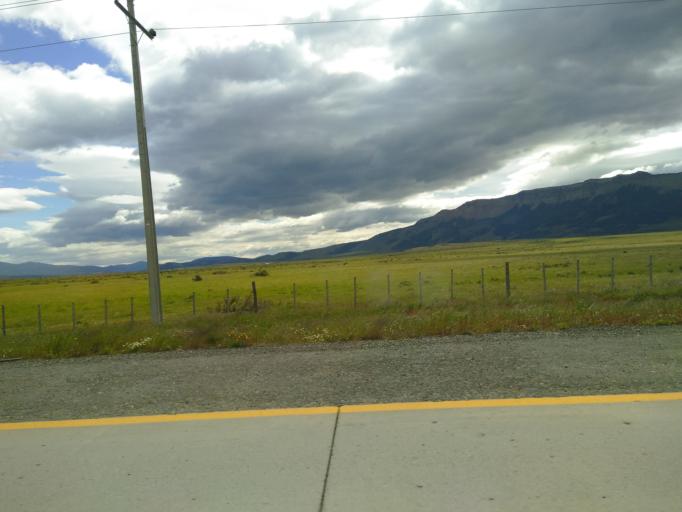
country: CL
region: Magallanes
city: Puerto Natales
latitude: -51.6660
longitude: -72.5279
